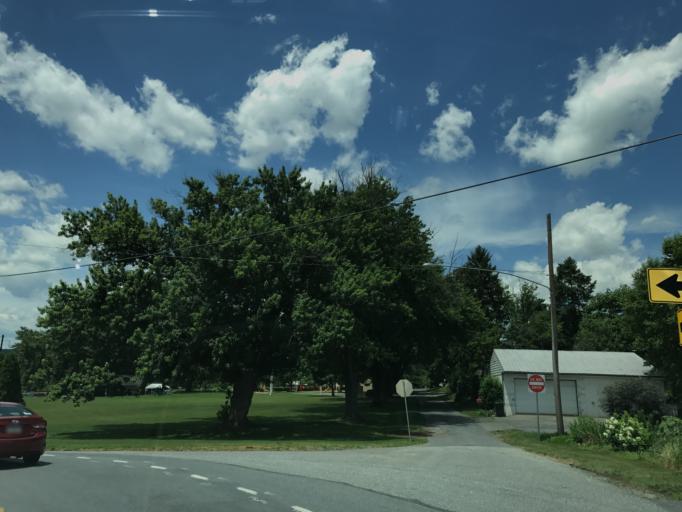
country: US
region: Pennsylvania
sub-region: Lancaster County
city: Columbia
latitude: 39.9903
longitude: -76.4674
